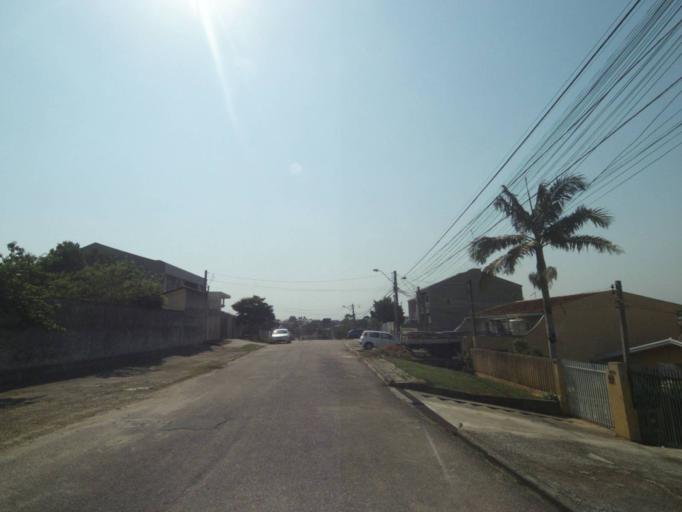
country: BR
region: Parana
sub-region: Sao Jose Dos Pinhais
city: Sao Jose dos Pinhais
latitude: -25.5088
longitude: -49.2722
